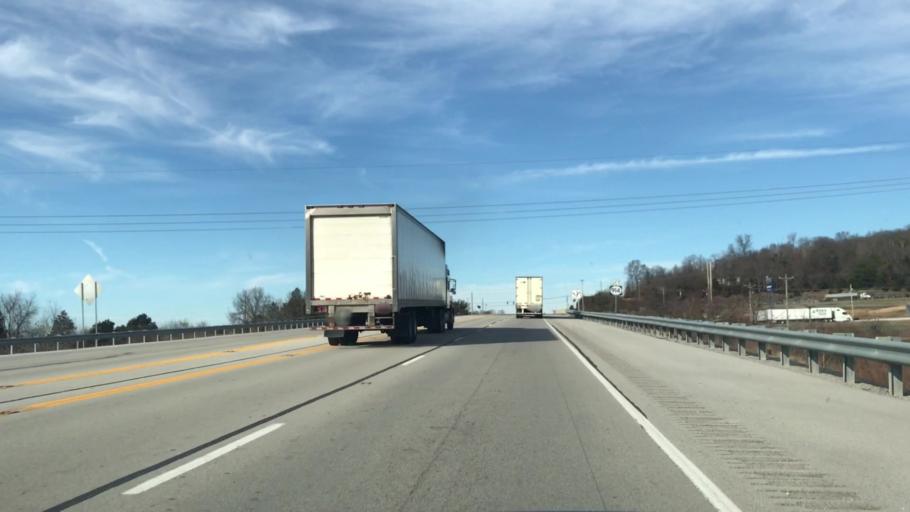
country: US
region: Kentucky
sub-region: Pulaski County
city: Somerset
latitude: 37.0478
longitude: -84.5854
